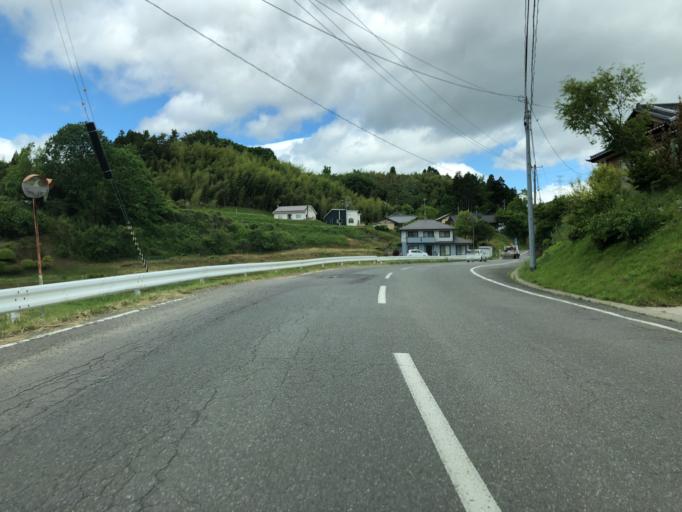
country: JP
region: Fukushima
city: Motomiya
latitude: 37.4874
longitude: 140.4383
